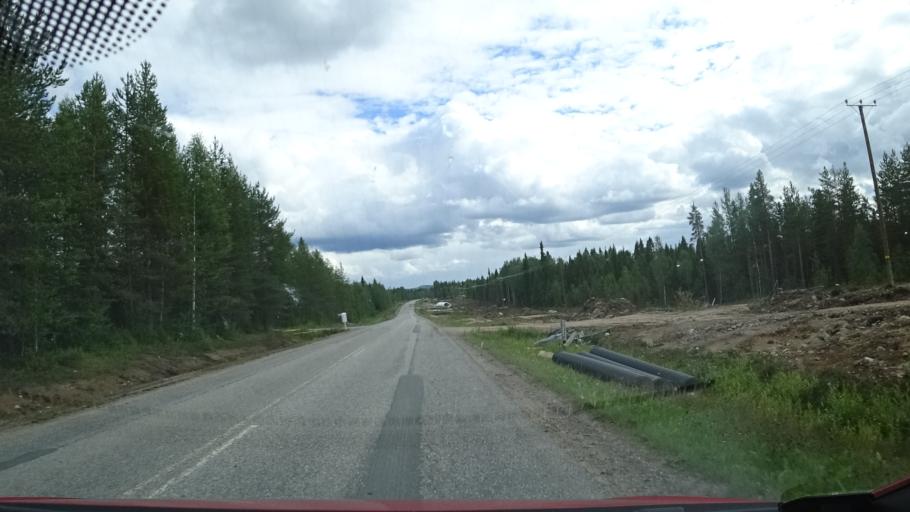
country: FI
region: Lapland
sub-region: Rovaniemi
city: Rovaniemi
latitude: 66.5404
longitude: 25.7179
